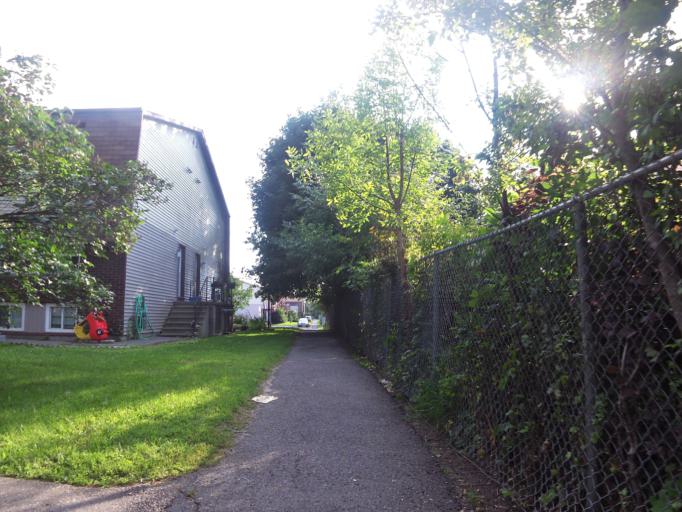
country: CA
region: Ontario
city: Bells Corners
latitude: 45.3339
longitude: -75.7588
